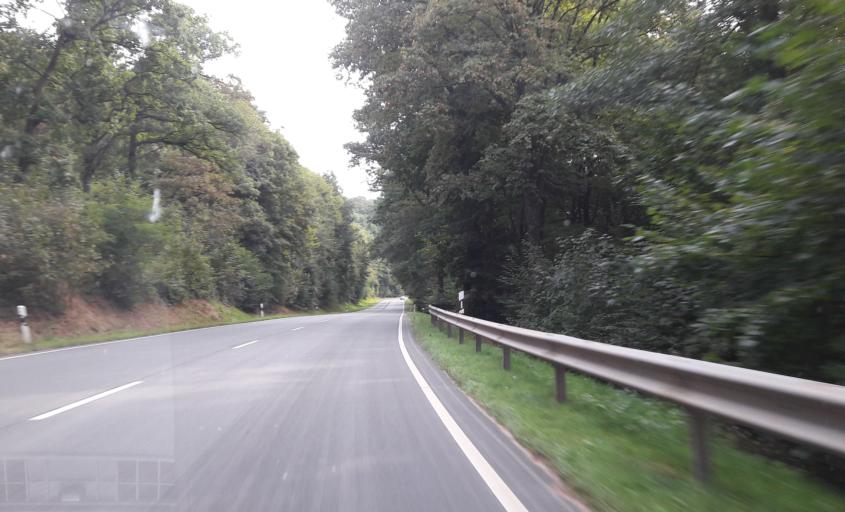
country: DE
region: Rheinland-Pfalz
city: Ellweiler
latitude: 49.6031
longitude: 7.1465
